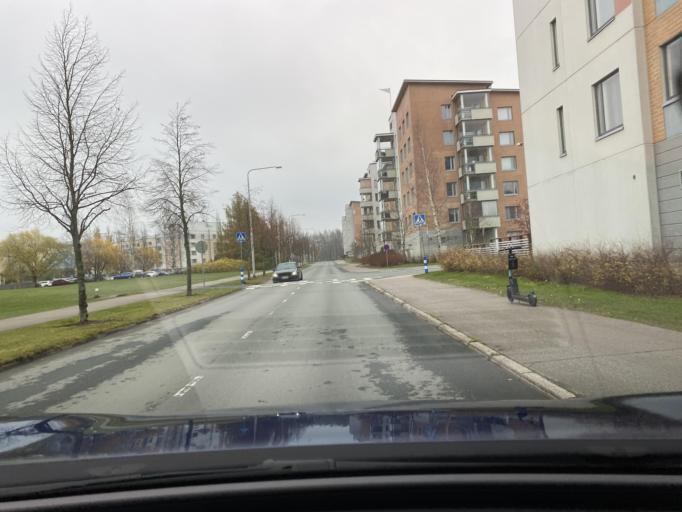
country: FI
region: Pirkanmaa
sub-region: Tampere
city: Nokia
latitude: 61.4679
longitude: 23.5256
